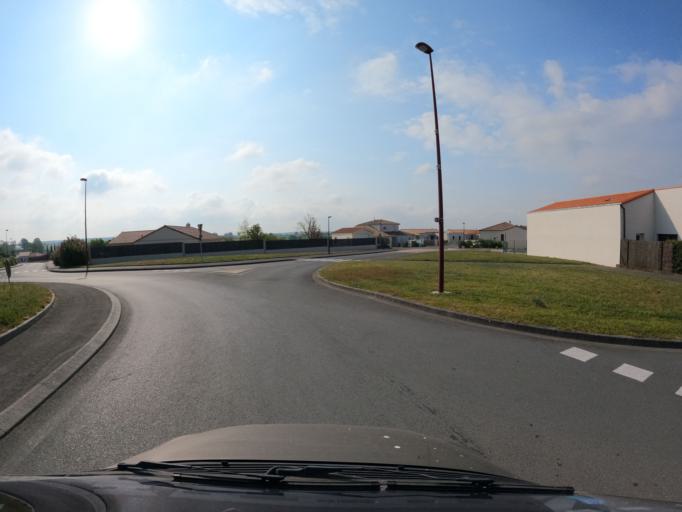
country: FR
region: Pays de la Loire
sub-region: Departement de Maine-et-Loire
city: Torfou
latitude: 47.0322
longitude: -1.1242
